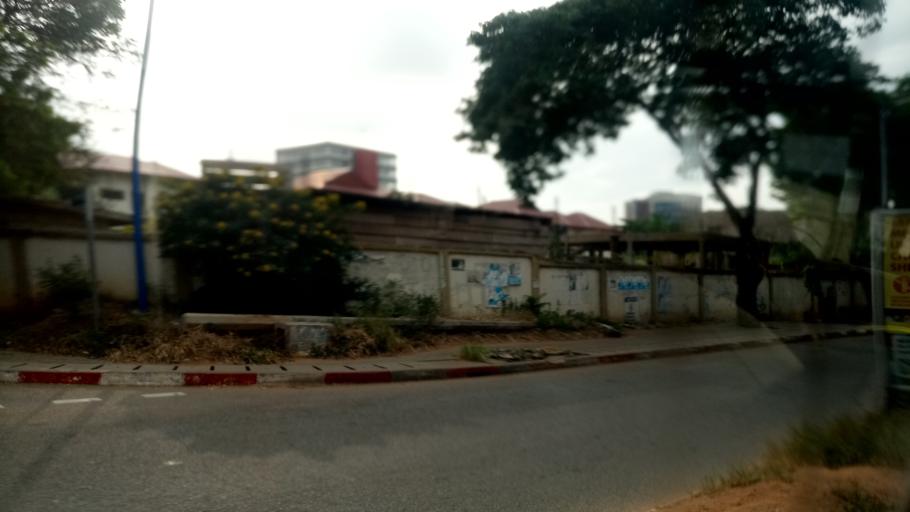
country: GH
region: Greater Accra
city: Accra
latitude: 5.5584
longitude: -0.1962
